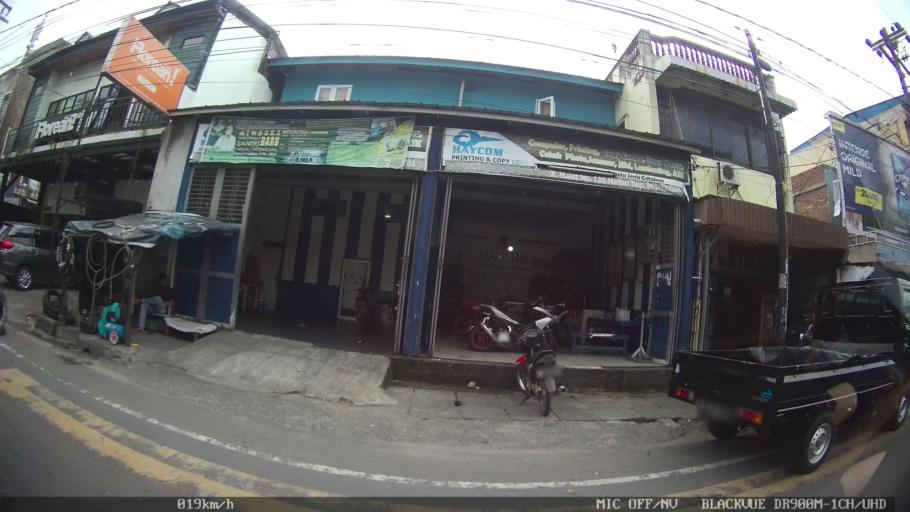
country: ID
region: North Sumatra
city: Medan
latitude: 3.5721
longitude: 98.6953
